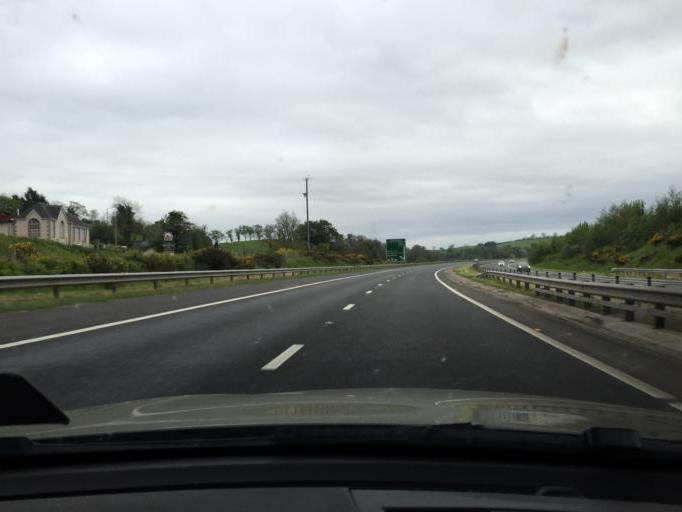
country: GB
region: Northern Ireland
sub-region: Newry and Mourne District
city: Newry
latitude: 54.2260
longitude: -6.3185
